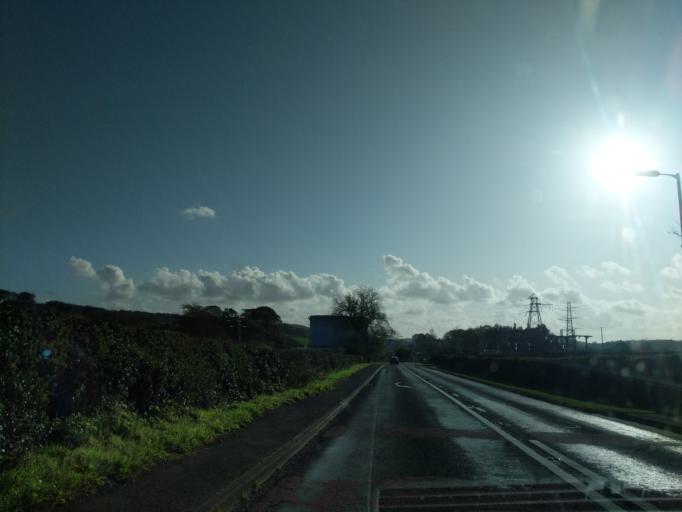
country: GB
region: Scotland
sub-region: Dumfries and Galloway
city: Kirkcudbright
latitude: 54.8626
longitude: -4.0326
